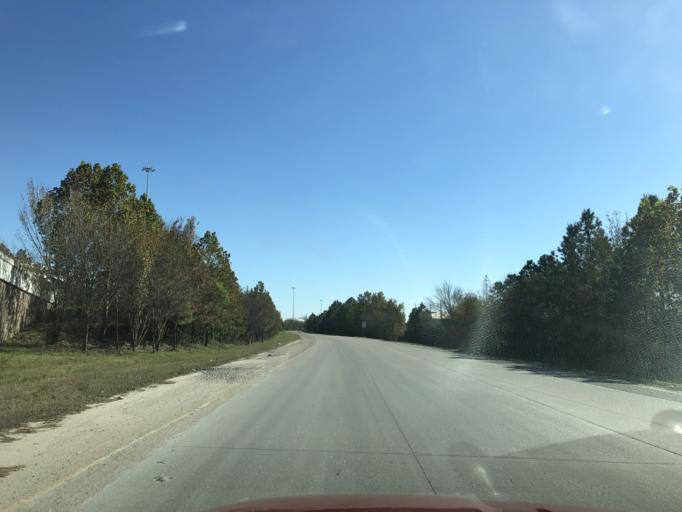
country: US
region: Texas
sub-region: Harris County
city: Cloverleaf
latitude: 29.7702
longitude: -95.1537
